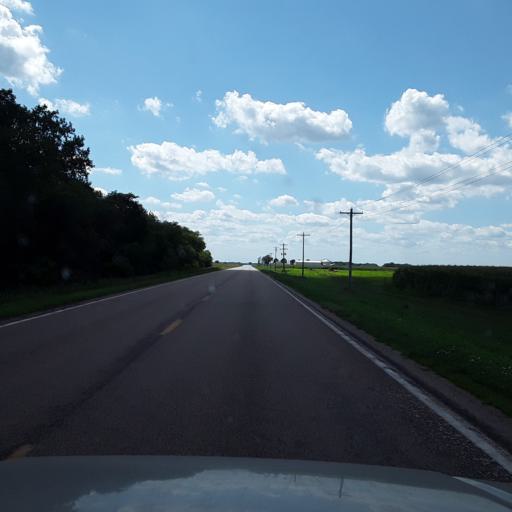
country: US
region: Nebraska
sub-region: Merrick County
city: Central City
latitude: 41.1910
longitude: -98.0265
